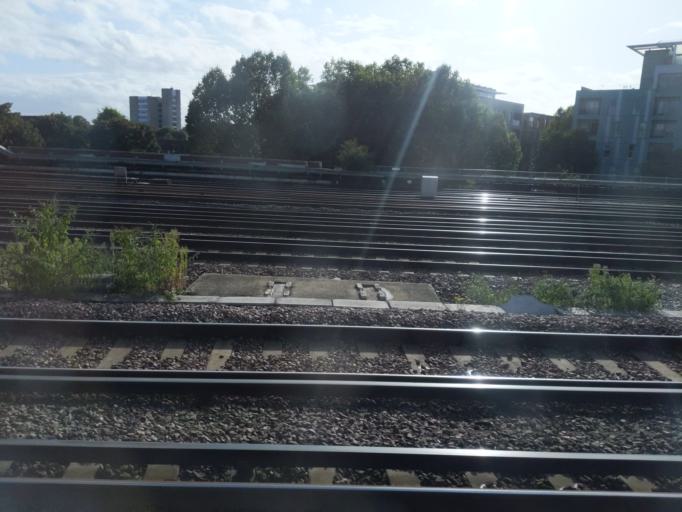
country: GB
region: England
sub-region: Greater London
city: City of London
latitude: 51.4965
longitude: -0.0692
